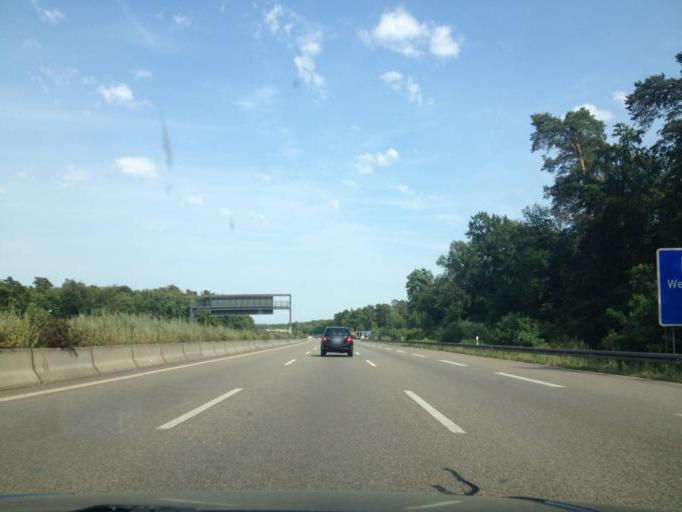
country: DE
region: Baden-Wuerttemberg
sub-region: Karlsruhe Region
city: Sankt Leon-Rot
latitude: 49.2737
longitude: 8.6433
